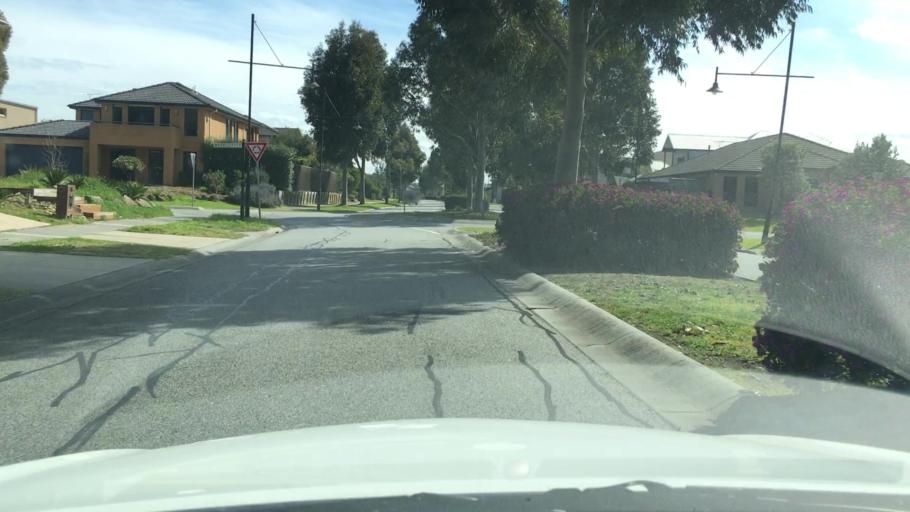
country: AU
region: Victoria
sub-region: Kingston
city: Waterways
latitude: -38.0168
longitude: 145.1321
